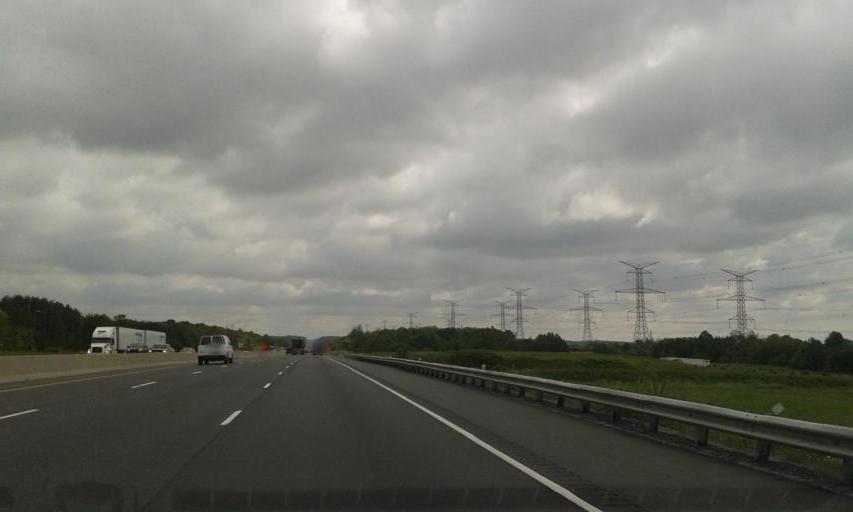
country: CA
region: Ontario
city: Cobourg
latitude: 43.9306
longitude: -78.4908
